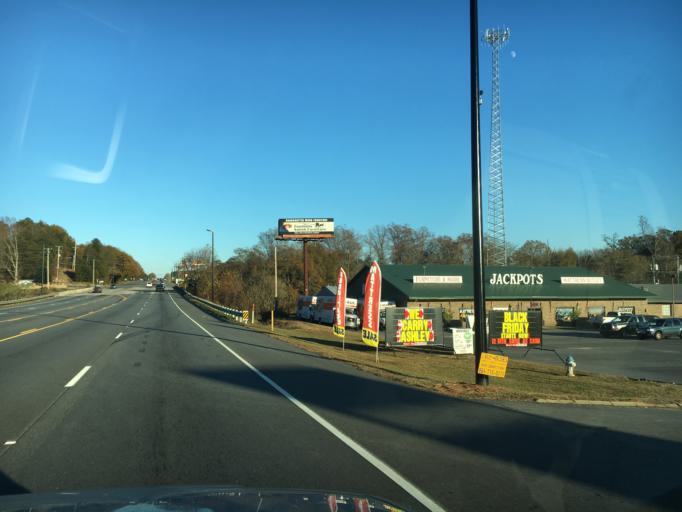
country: US
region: South Carolina
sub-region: Greenville County
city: Greer
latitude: 34.9509
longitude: -82.1878
